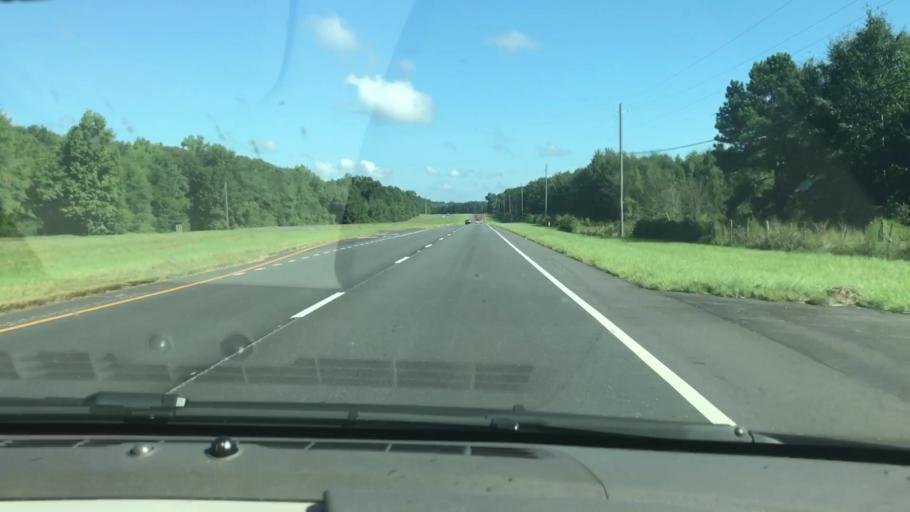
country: US
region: Alabama
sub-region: Barbour County
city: Eufaula
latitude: 32.0089
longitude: -85.1165
